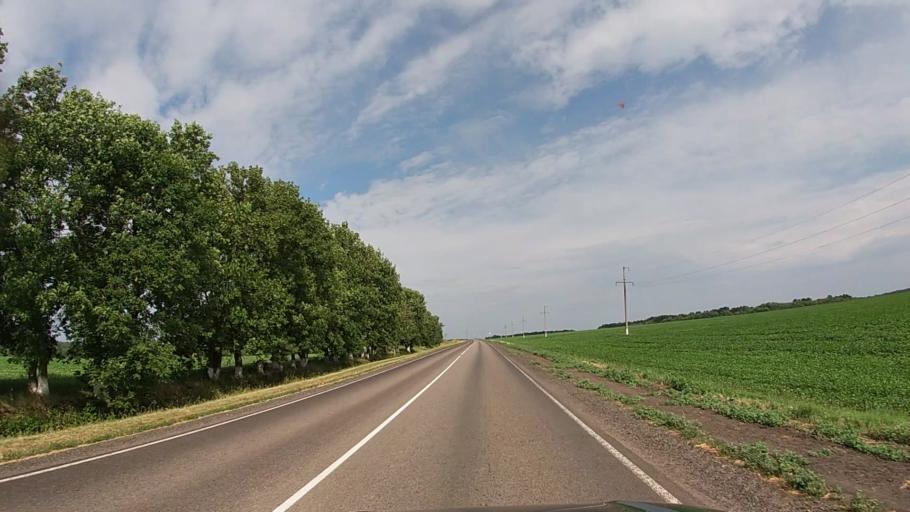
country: RU
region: Belgorod
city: Krasnaya Yaruga
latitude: 50.8062
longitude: 35.5455
